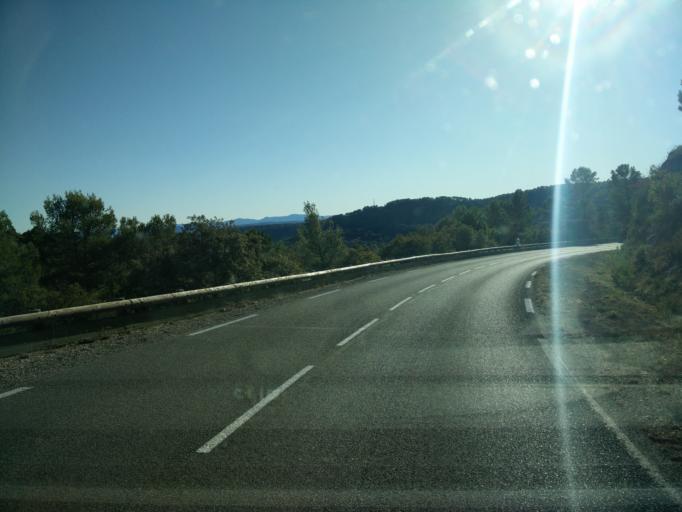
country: FR
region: Provence-Alpes-Cote d'Azur
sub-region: Departement du Var
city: Salernes
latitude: 43.5792
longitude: 6.2229
